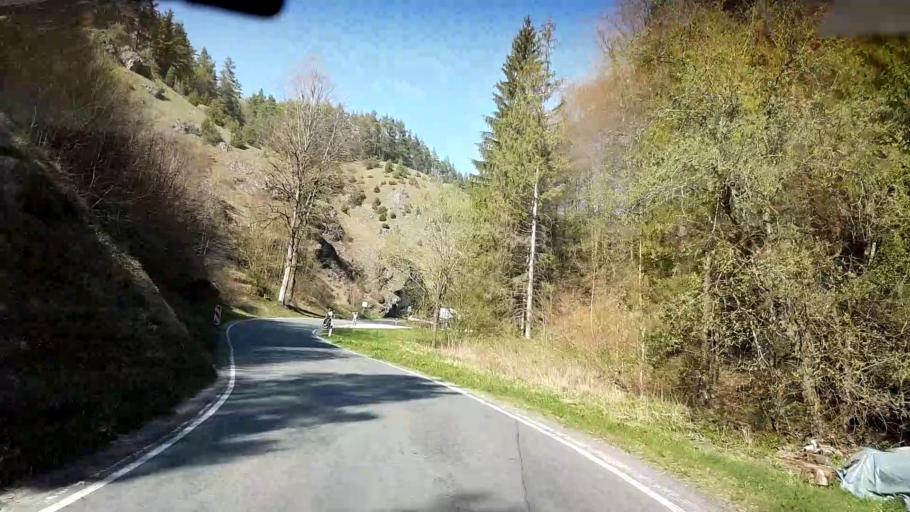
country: DE
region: Bavaria
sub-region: Upper Franconia
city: Pottenstein
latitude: 49.7762
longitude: 11.4156
